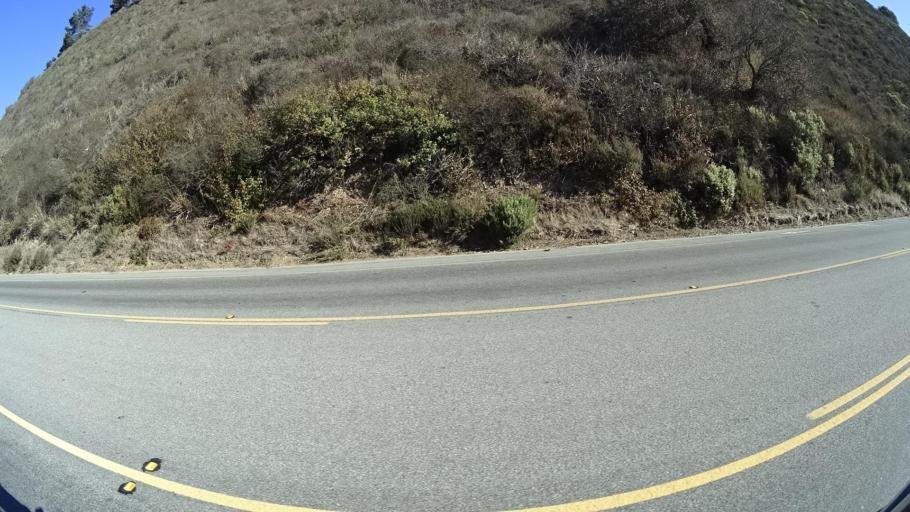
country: US
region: California
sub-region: Monterey County
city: Del Rey Oaks
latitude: 36.5335
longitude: -121.8484
